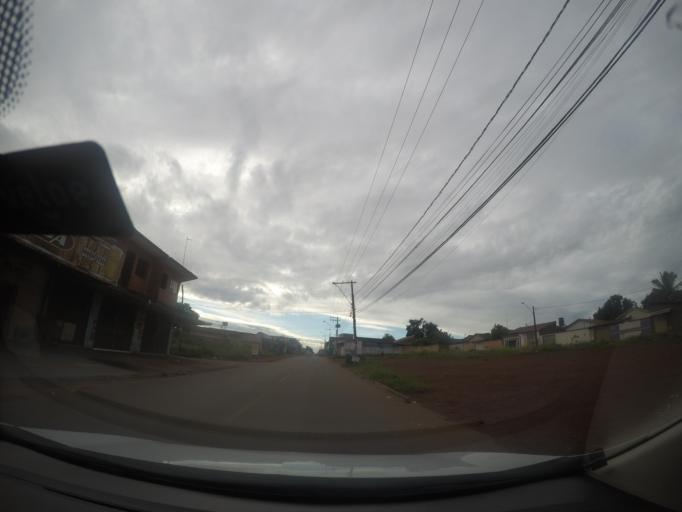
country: BR
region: Goias
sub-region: Goiania
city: Goiania
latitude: -16.6024
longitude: -49.3255
